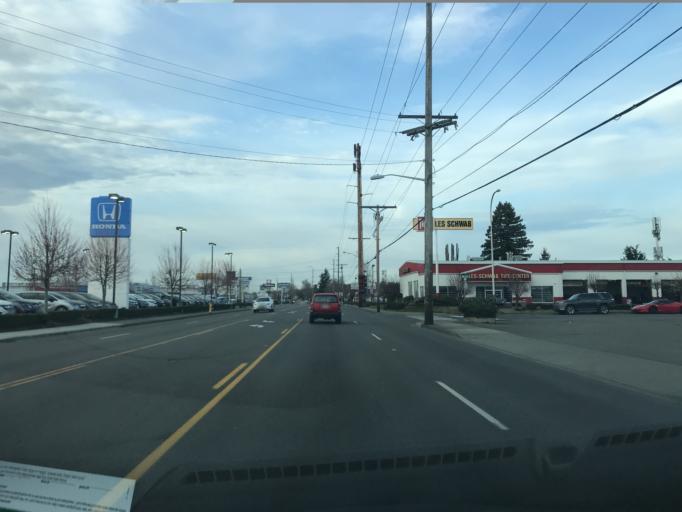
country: US
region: Washington
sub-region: King County
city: Auburn
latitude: 47.3298
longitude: -122.2215
